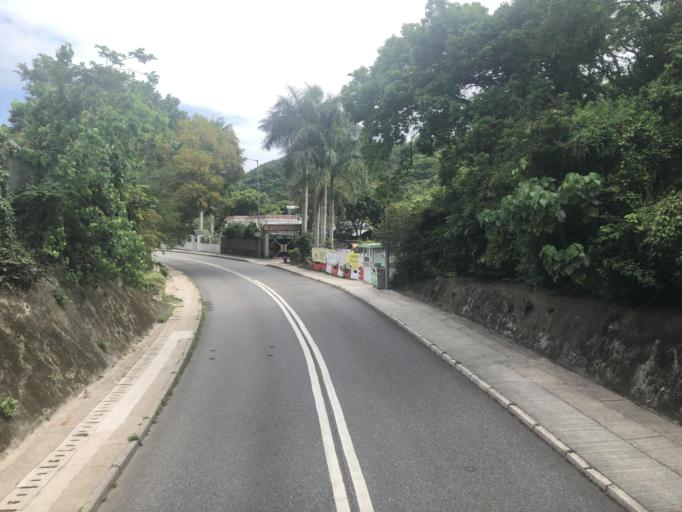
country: HK
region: Sai Kung
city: Sai Kung
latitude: 22.3908
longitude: 114.3004
